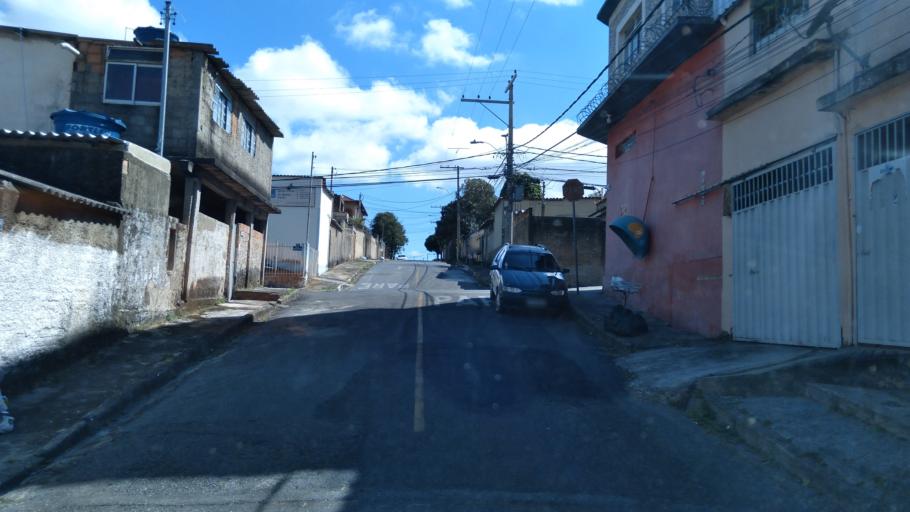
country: BR
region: Minas Gerais
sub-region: Belo Horizonte
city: Belo Horizonte
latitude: -19.8795
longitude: -43.9226
